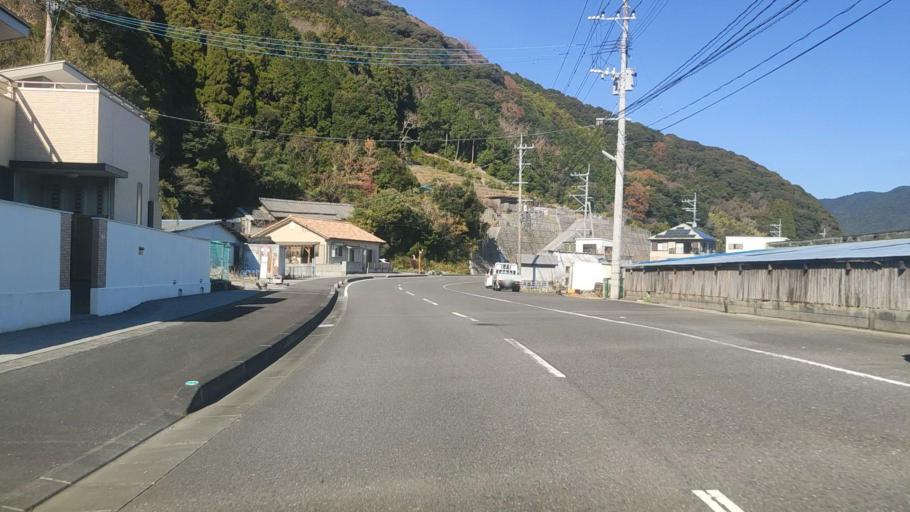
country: JP
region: Oita
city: Saiki
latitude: 32.8279
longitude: 131.9598
